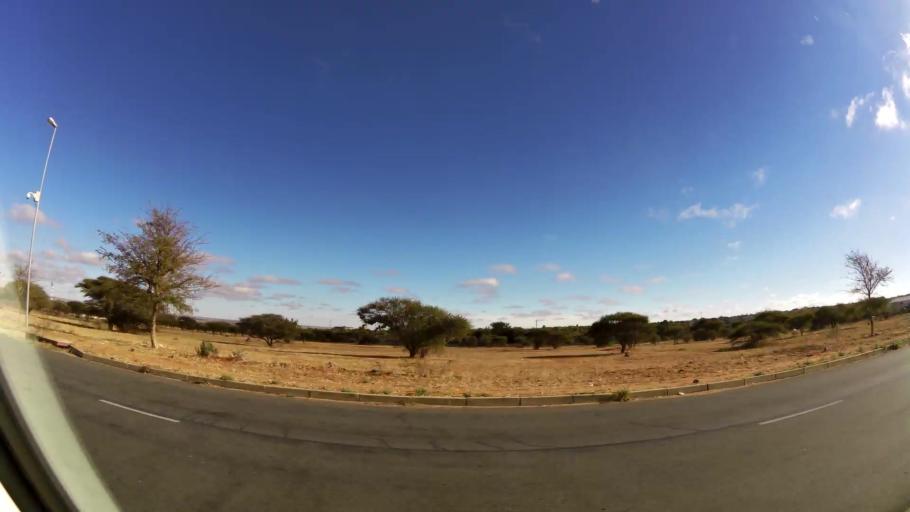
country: ZA
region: Limpopo
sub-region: Capricorn District Municipality
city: Polokwane
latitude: -23.9222
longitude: 29.4741
